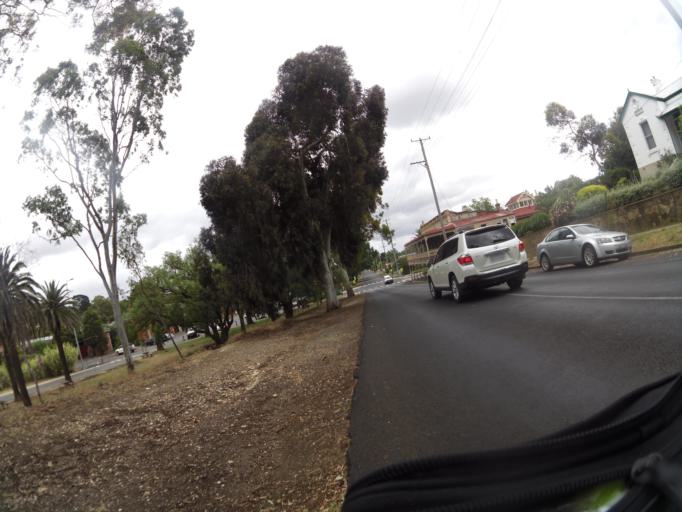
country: AU
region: Victoria
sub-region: Mount Alexander
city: Castlemaine
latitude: -37.0637
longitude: 144.2145
